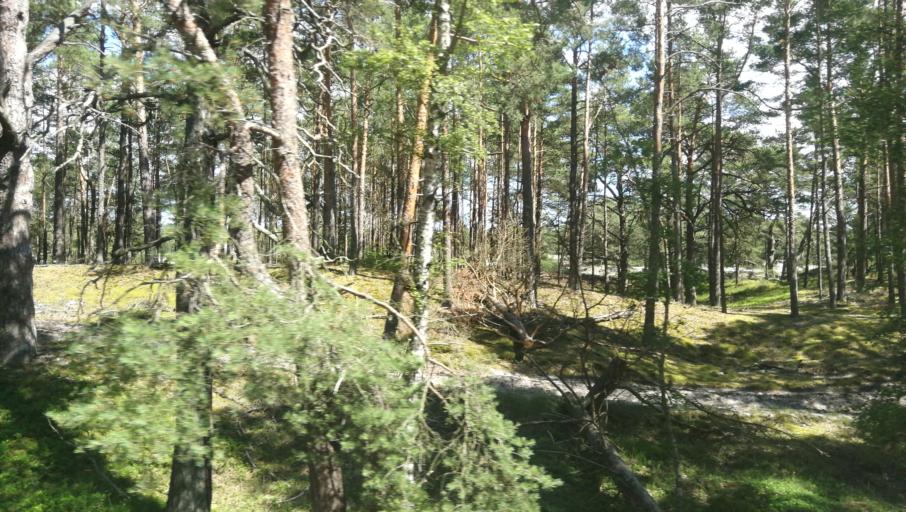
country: PL
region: Pomeranian Voivodeship
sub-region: Powiat pucki
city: Hel
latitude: 54.6222
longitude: 18.8040
